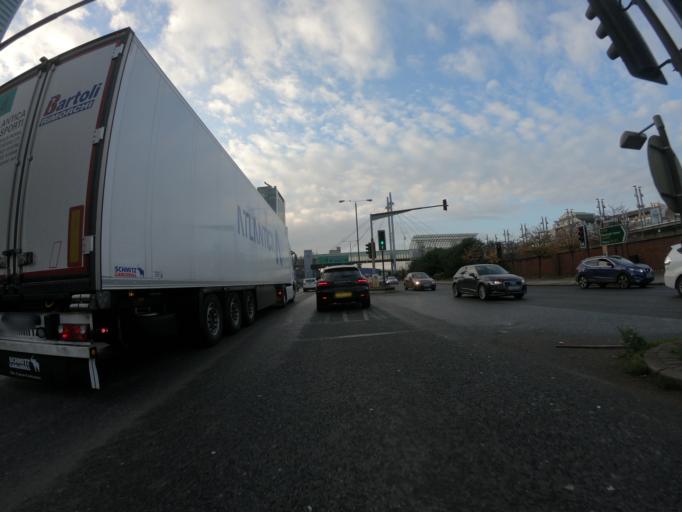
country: GB
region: England
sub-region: Greater London
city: Poplar
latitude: 51.5073
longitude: -0.0163
